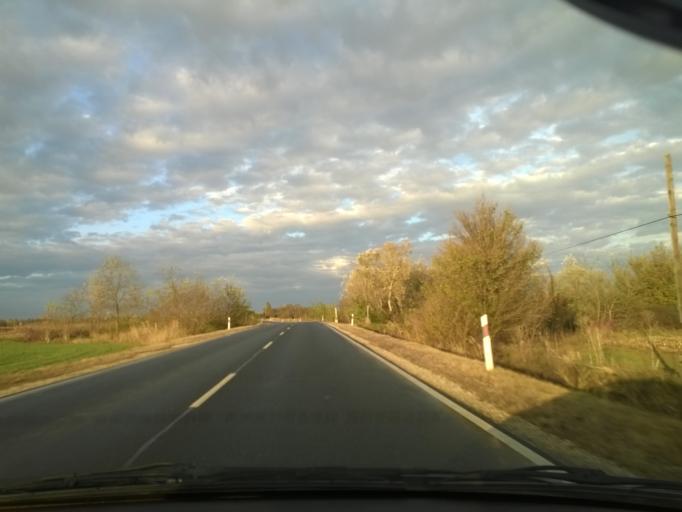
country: HU
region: Bacs-Kiskun
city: Dunapataj
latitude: 46.6289
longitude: 18.9987
